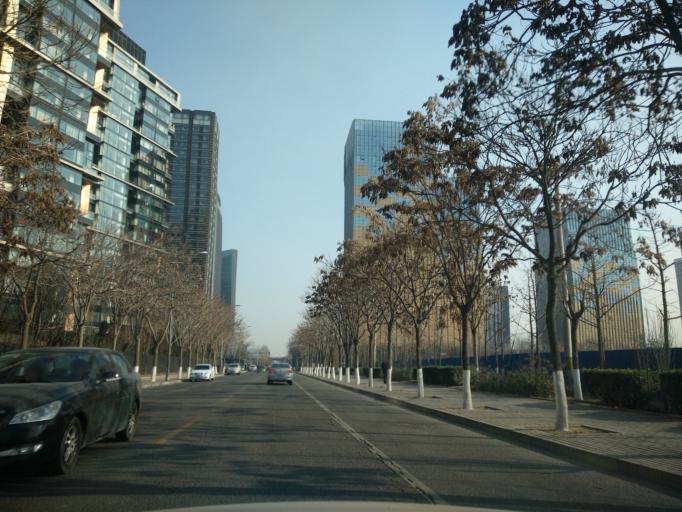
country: CN
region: Beijing
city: Jiugong
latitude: 39.7873
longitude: 116.5037
